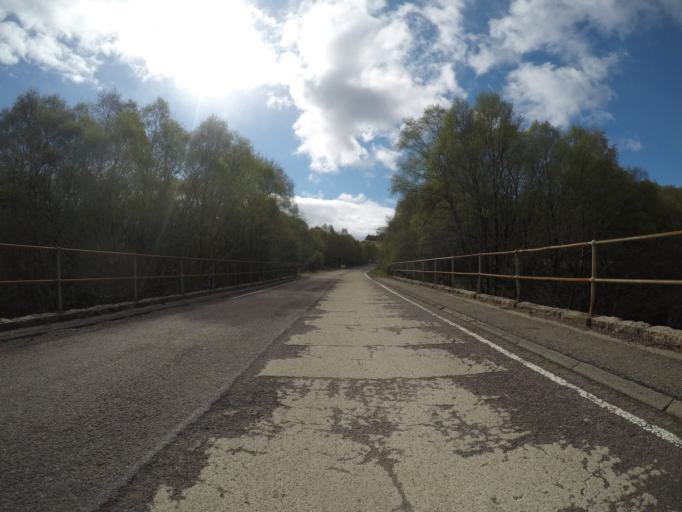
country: GB
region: Scotland
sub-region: Highland
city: Spean Bridge
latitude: 57.1457
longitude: -4.9583
